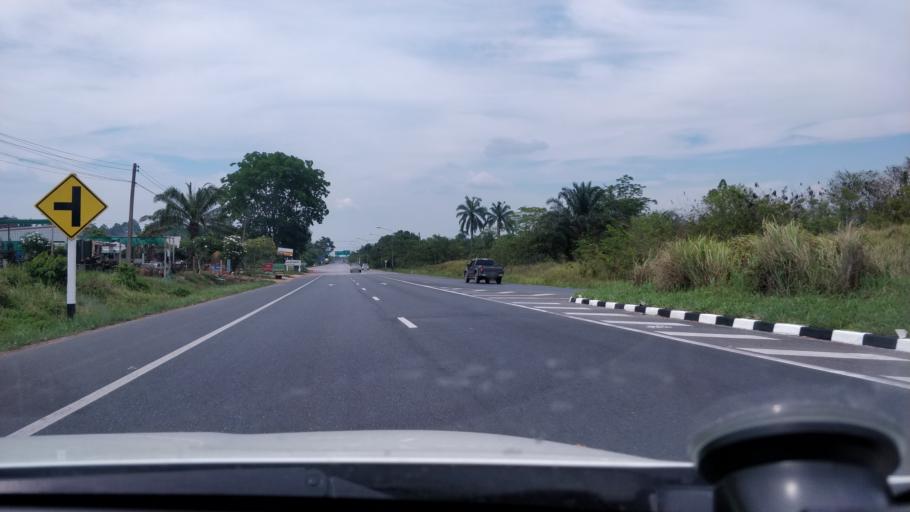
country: TH
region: Surat Thani
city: Khian Sa
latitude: 8.8348
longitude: 99.1748
